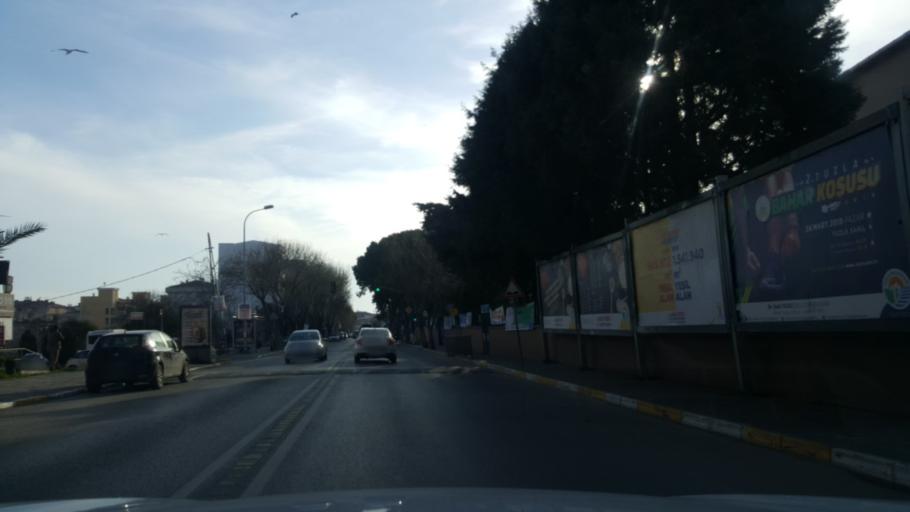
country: TR
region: Istanbul
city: Icmeler
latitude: 40.8210
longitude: 29.3084
